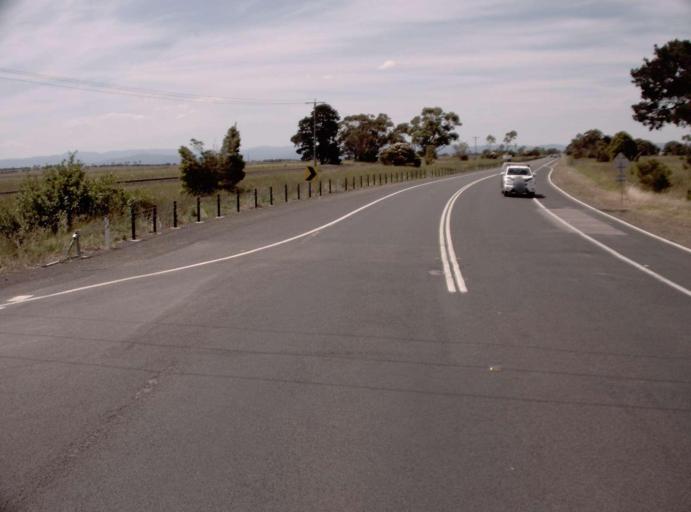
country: AU
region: Victoria
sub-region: Wellington
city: Sale
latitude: -38.0323
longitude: 147.0579
